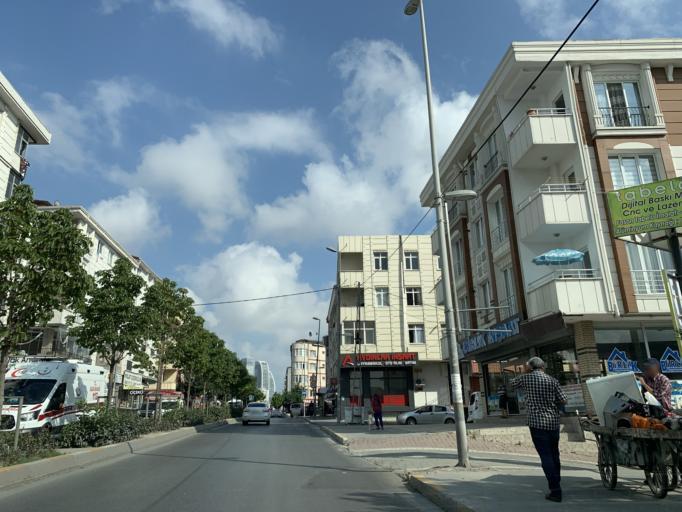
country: TR
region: Istanbul
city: Esenyurt
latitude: 41.0255
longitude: 28.6690
